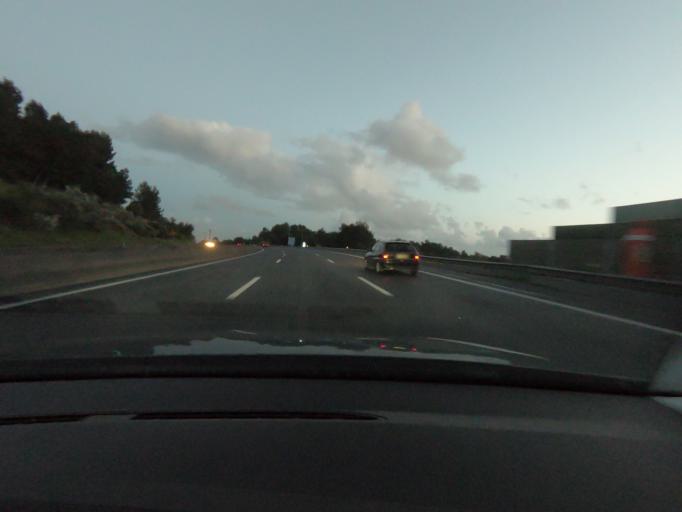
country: PT
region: Lisbon
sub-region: Oeiras
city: Quejas
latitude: 38.7231
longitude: -9.2734
